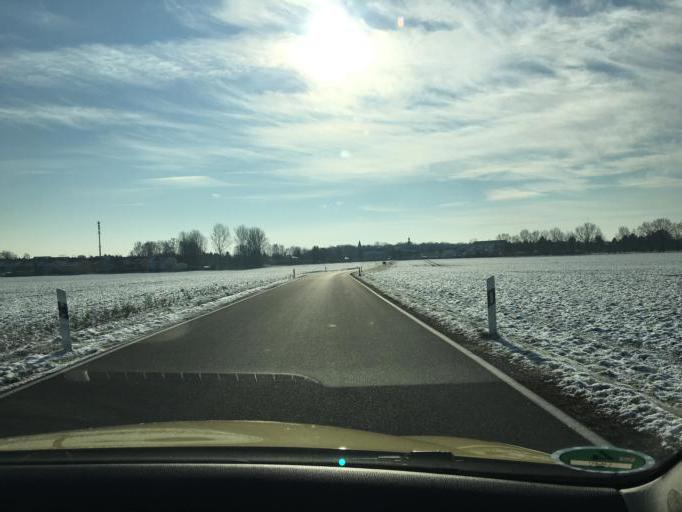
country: DE
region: Saxony
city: Belgershain
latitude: 51.2418
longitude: 12.5466
